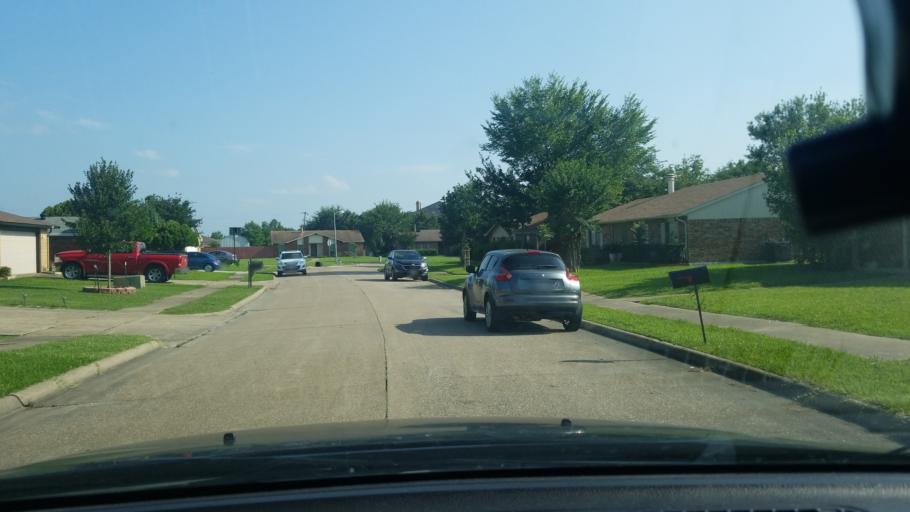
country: US
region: Texas
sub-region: Dallas County
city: Sunnyvale
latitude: 32.8170
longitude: -96.6037
